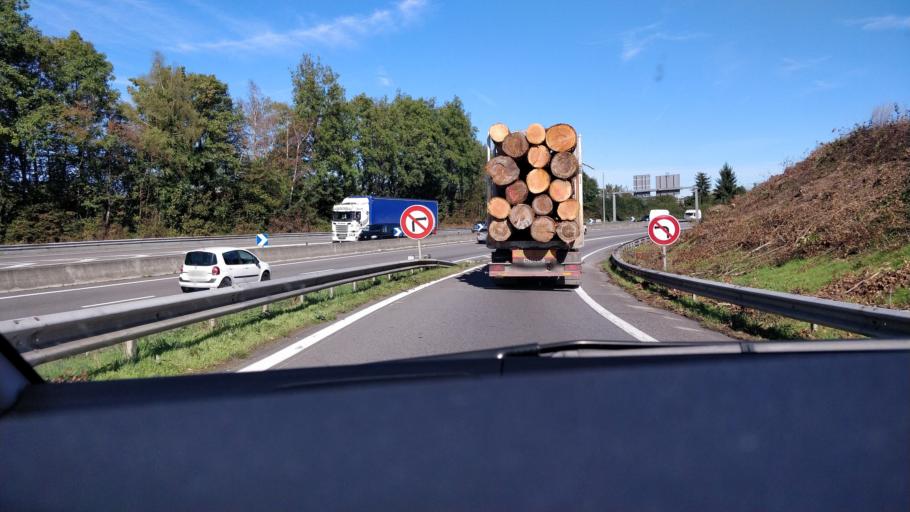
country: FR
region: Limousin
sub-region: Departement de la Haute-Vienne
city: Limoges
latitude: 45.8298
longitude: 1.2824
